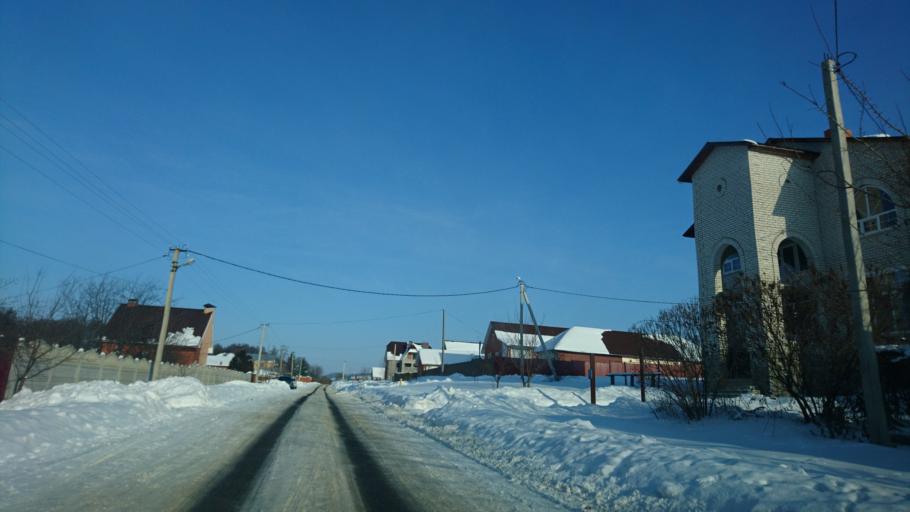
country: RU
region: Belgorod
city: Severnyy
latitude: 50.7229
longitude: 36.6104
